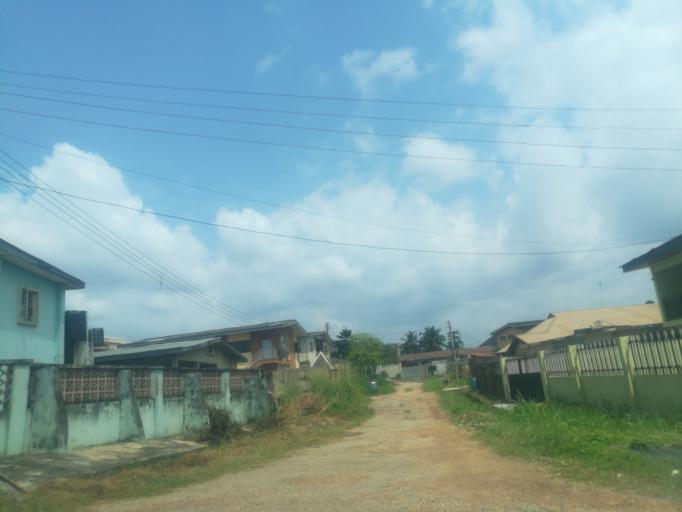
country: NG
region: Oyo
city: Ibadan
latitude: 7.3611
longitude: 3.8555
